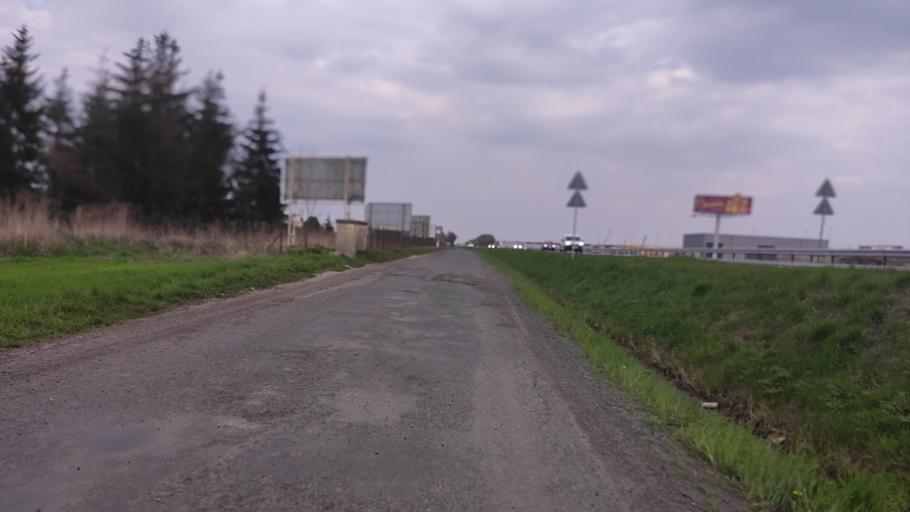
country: PL
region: Greater Poland Voivodeship
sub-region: Powiat poznanski
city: Swarzedz
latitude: 52.4019
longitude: 17.1264
